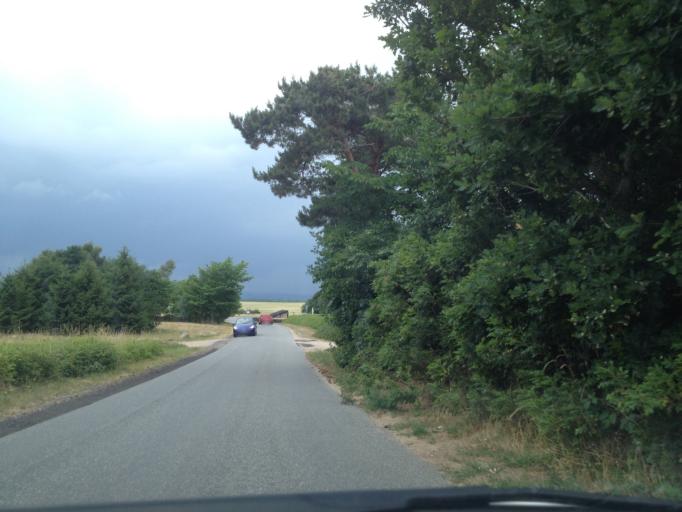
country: DK
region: Central Jutland
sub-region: Syddjurs Kommune
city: Ebeltoft
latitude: 56.1697
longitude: 10.6721
